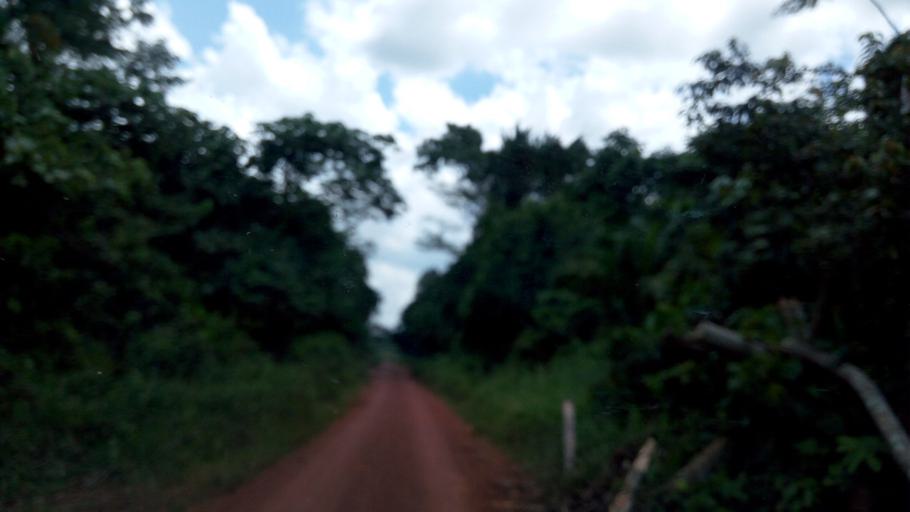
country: CD
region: Equateur
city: Libenge
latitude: 3.7706
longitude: 18.9586
